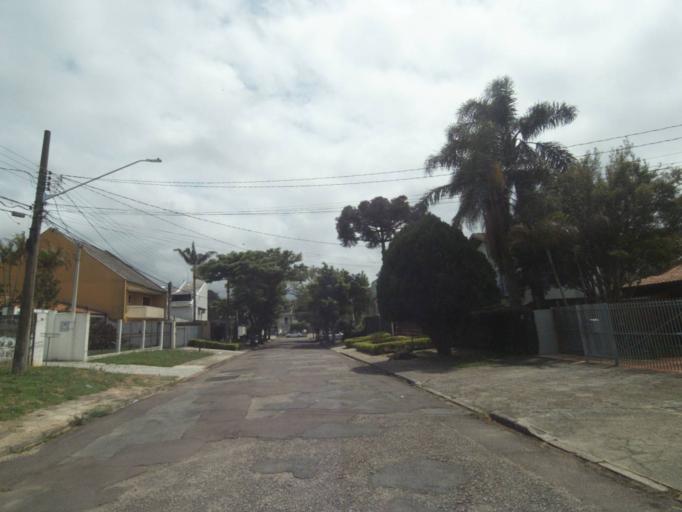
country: BR
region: Parana
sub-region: Pinhais
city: Pinhais
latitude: -25.4326
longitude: -49.2249
